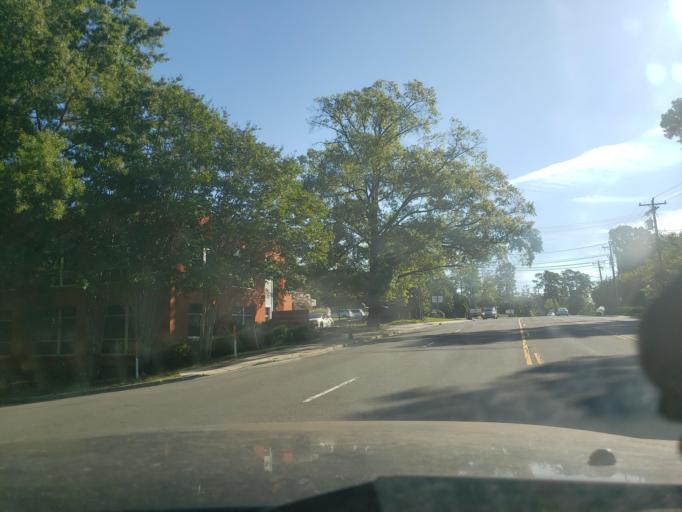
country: US
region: North Carolina
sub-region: Durham County
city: Durham
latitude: 35.9670
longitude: -78.9494
